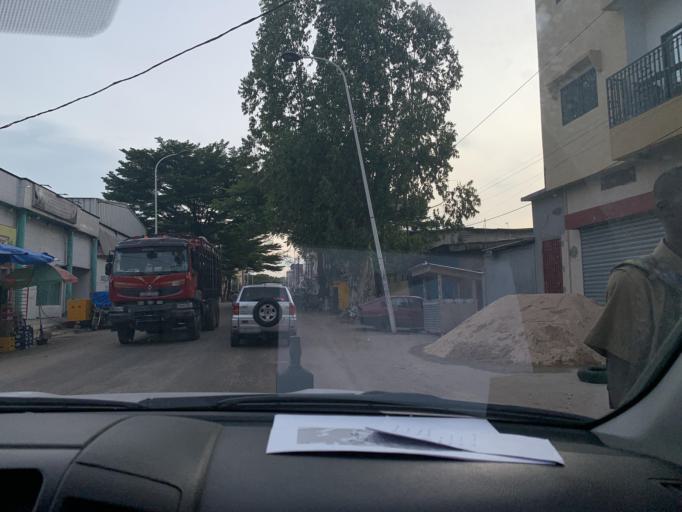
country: CG
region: Brazzaville
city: Brazzaville
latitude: -4.2642
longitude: 15.2878
